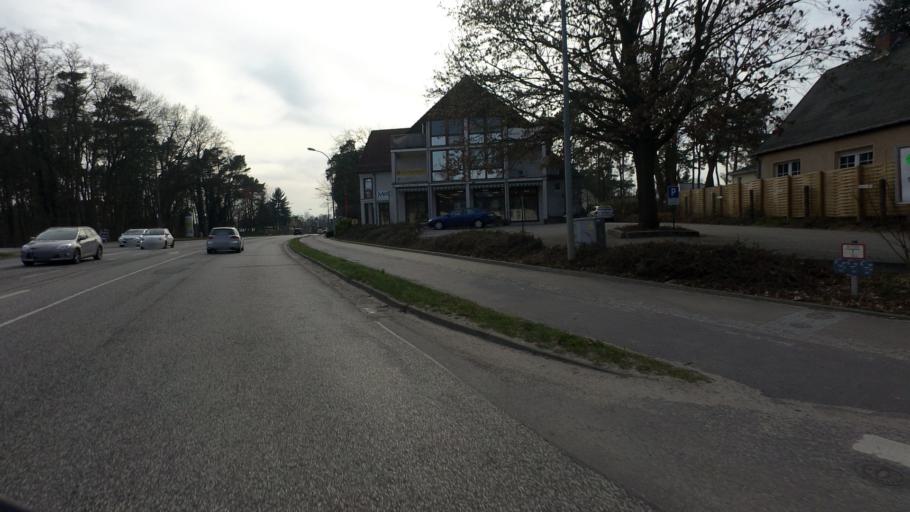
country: DE
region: Brandenburg
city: Stahnsdorf
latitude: 52.3888
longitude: 13.2035
